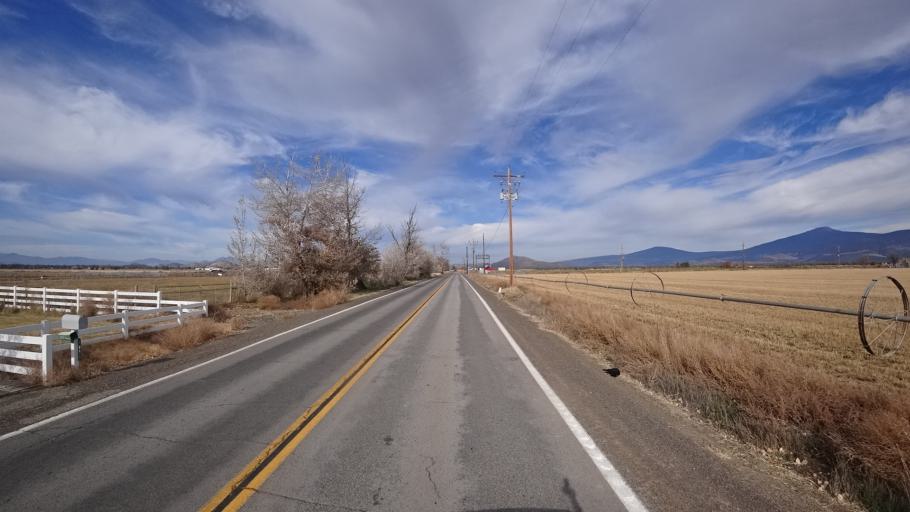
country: US
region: California
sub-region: Siskiyou County
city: Montague
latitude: 41.6148
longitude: -122.3996
